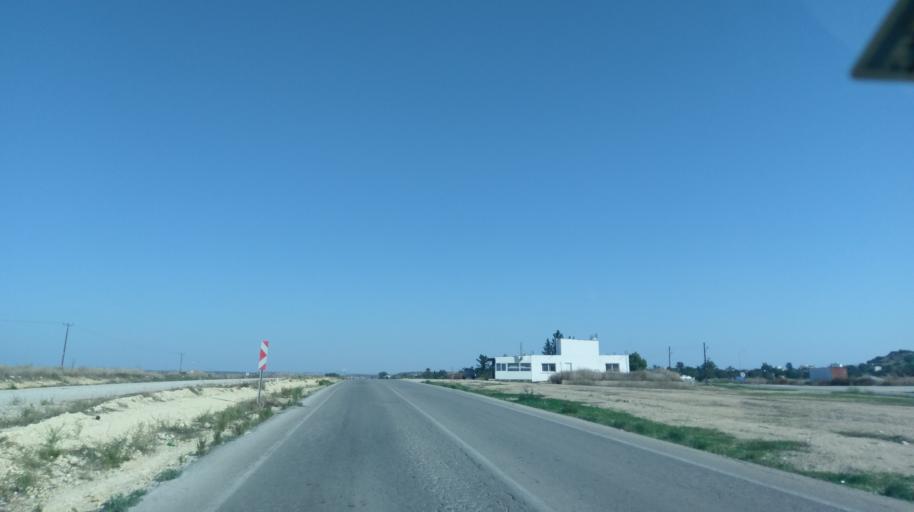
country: CY
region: Ammochostos
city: Trikomo
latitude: 35.3628
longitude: 34.0170
